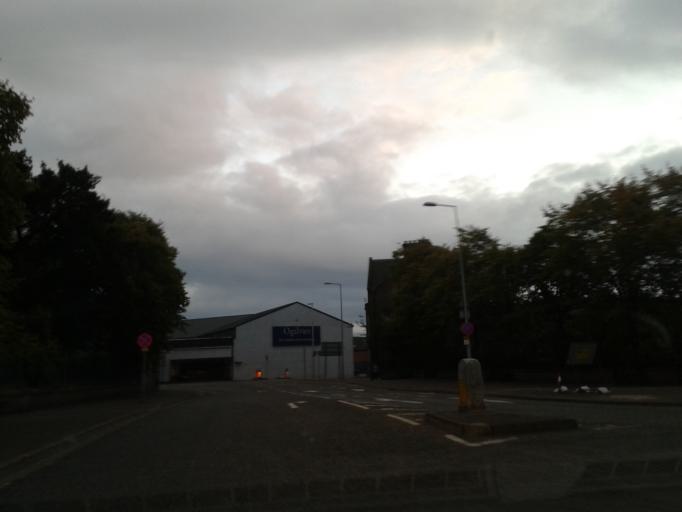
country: GB
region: Scotland
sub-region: Highland
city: Inverness
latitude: 57.4826
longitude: -4.2303
